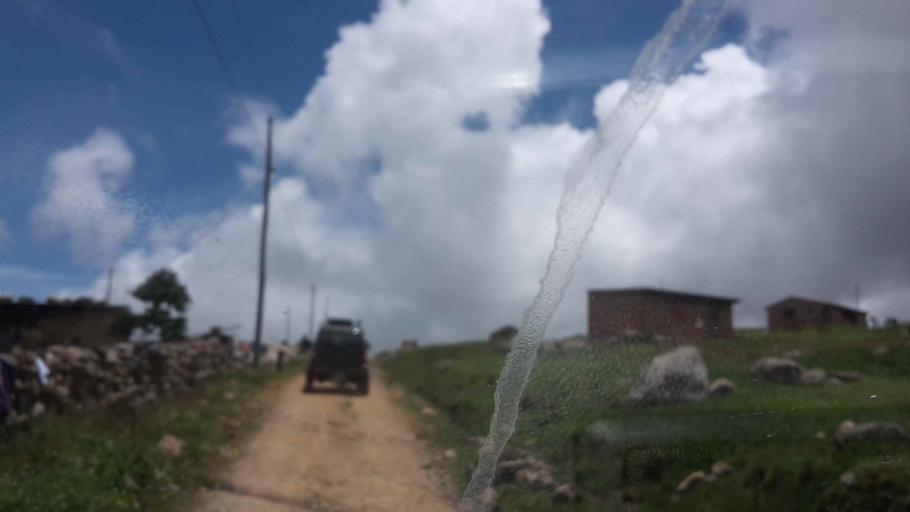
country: BO
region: Cochabamba
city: Cochabamba
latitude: -17.1822
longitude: -66.0598
